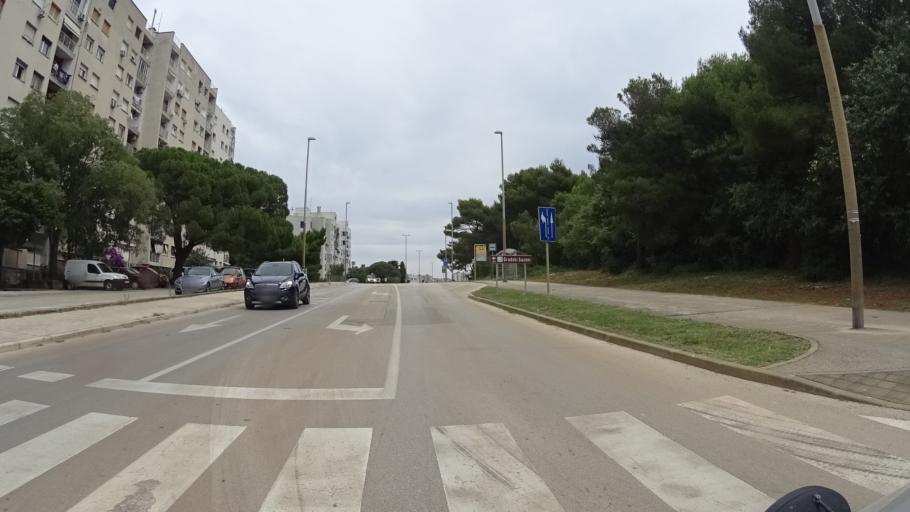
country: HR
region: Istarska
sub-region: Grad Pula
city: Pula
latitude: 44.8575
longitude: 13.8302
